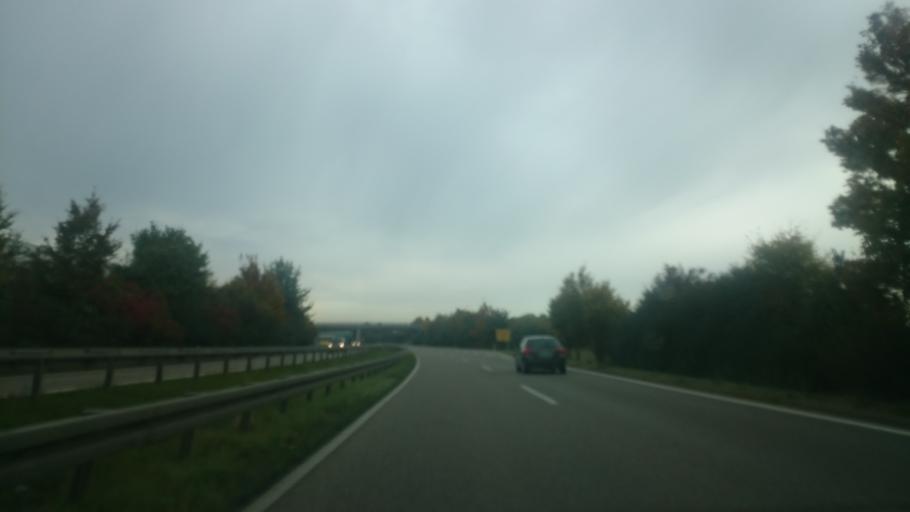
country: DE
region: Bavaria
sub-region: Swabia
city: Westendorf
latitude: 48.5701
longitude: 10.8475
